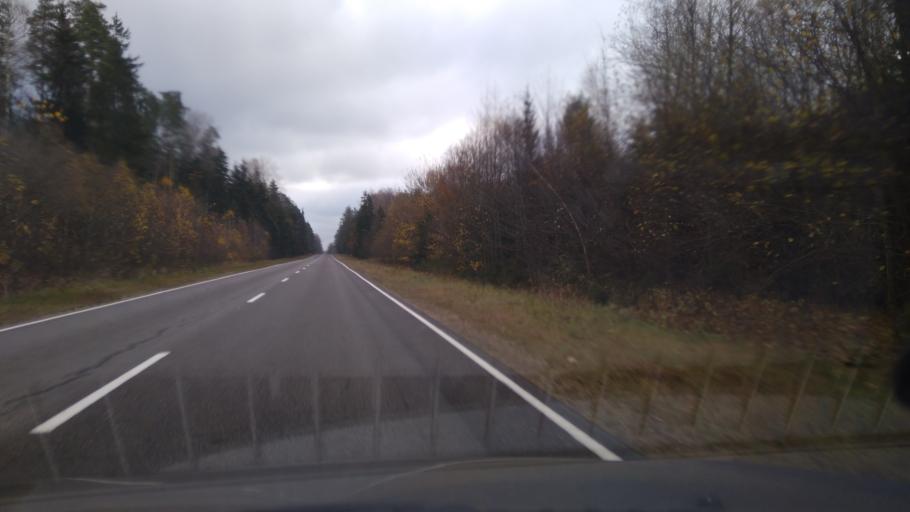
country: BY
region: Minsk
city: Urechcha
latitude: 53.2134
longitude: 27.8721
